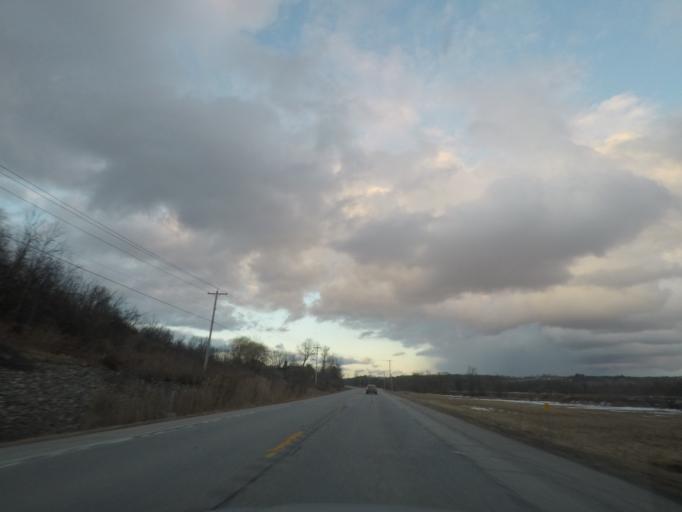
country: US
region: New York
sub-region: Montgomery County
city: Fonda
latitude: 42.9259
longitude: -74.4367
